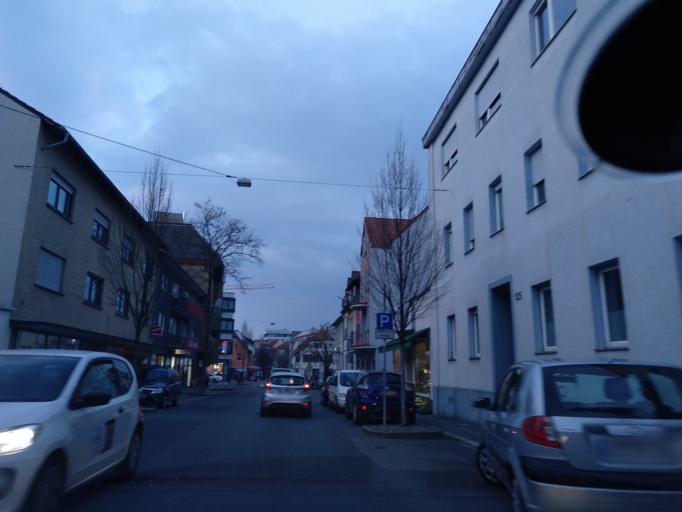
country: DE
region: Baden-Wuerttemberg
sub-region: Karlsruhe Region
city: Wiesloch
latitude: 49.2923
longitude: 8.6974
